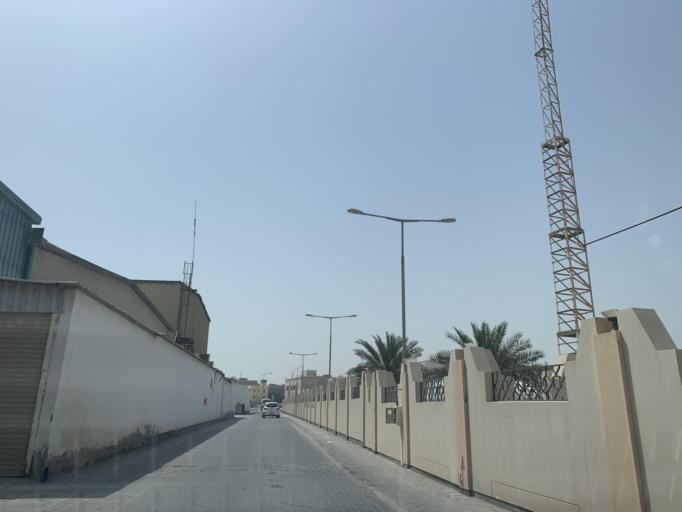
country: BH
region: Northern
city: Madinat `Isa
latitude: 26.1843
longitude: 50.5486
